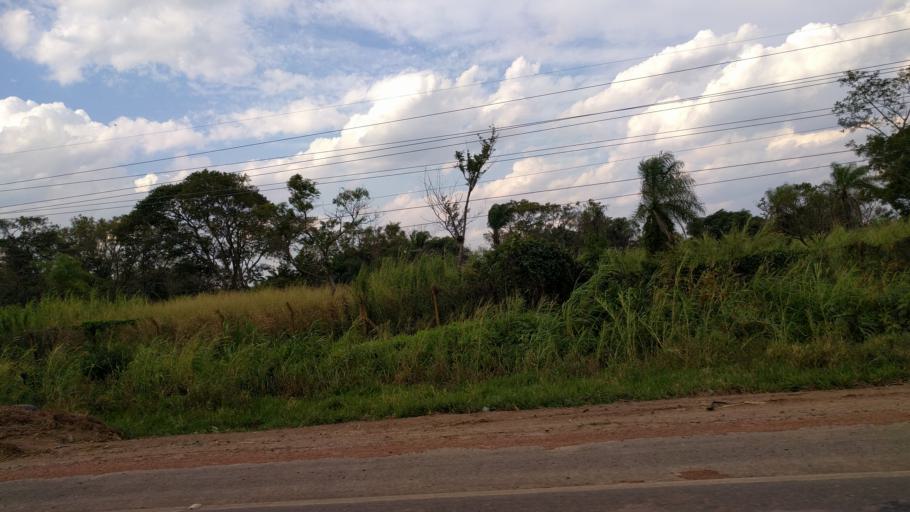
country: BO
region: Santa Cruz
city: Warnes
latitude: -17.4388
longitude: -63.1920
